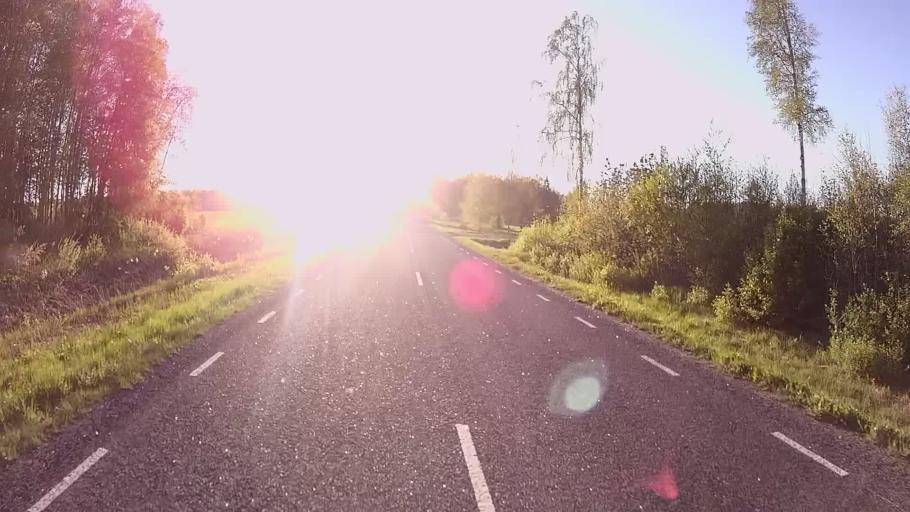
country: EE
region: Jogevamaa
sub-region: Poltsamaa linn
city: Poltsamaa
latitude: 58.5238
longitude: 25.9638
